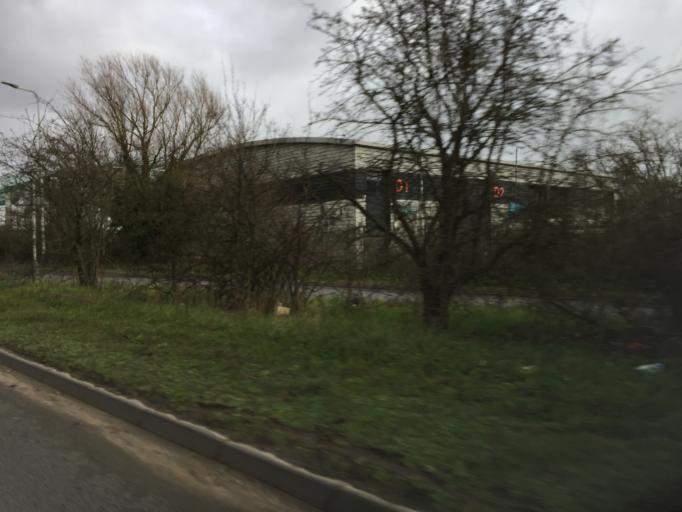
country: GB
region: England
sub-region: West Berkshire
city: Theale
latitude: 51.4340
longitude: -1.0790
